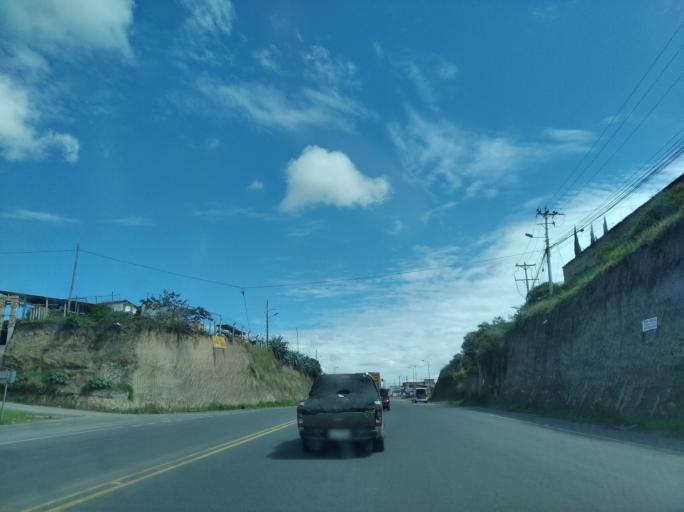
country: EC
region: Pichincha
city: Sangolqui
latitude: -0.1793
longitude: -78.3296
